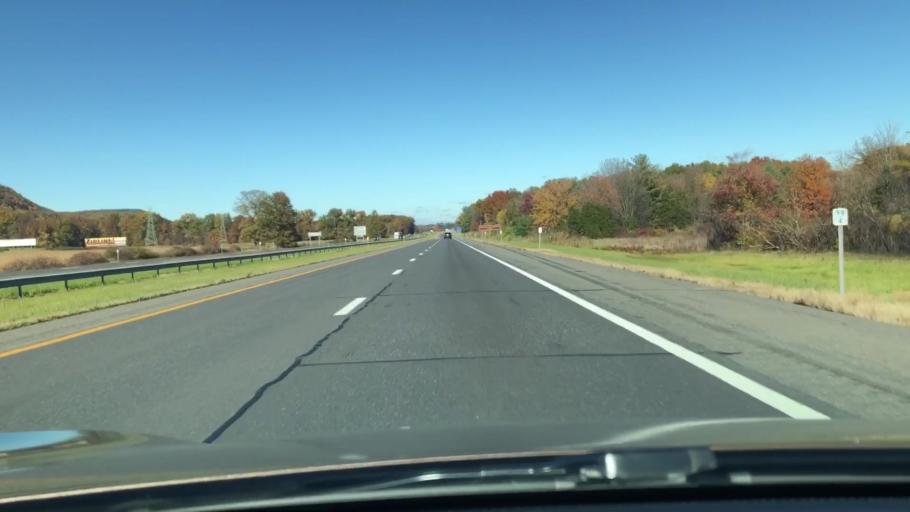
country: US
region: New York
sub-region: Ulster County
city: Glasco
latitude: 42.0437
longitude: -73.9876
